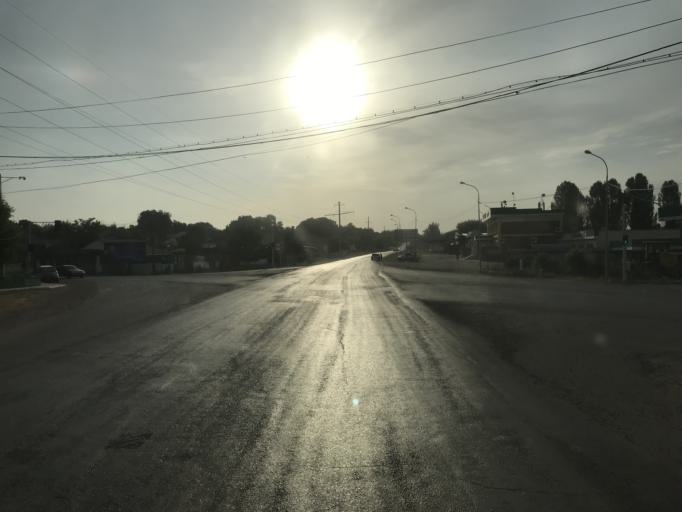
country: KZ
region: Ongtustik Qazaqstan
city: Saryaghash
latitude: 41.4897
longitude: 69.2606
